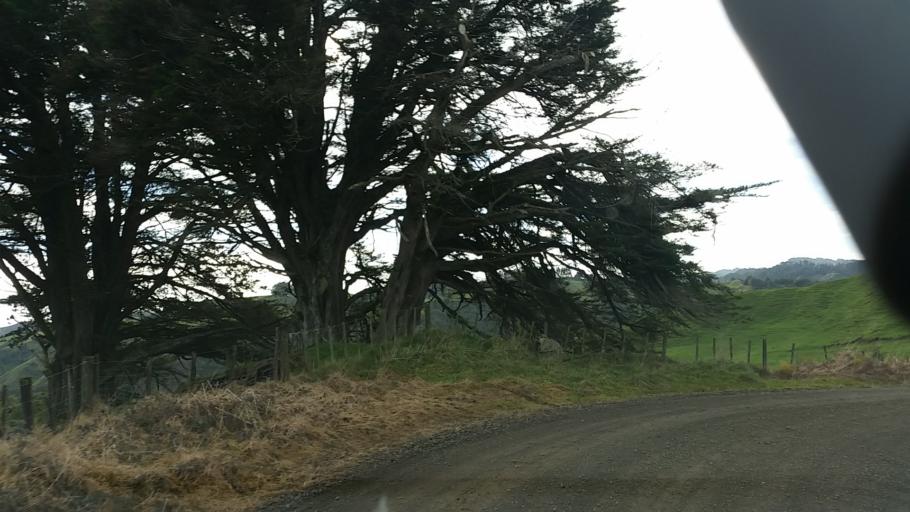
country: NZ
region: Taranaki
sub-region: New Plymouth District
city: Waitara
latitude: -39.0629
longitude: 174.3821
